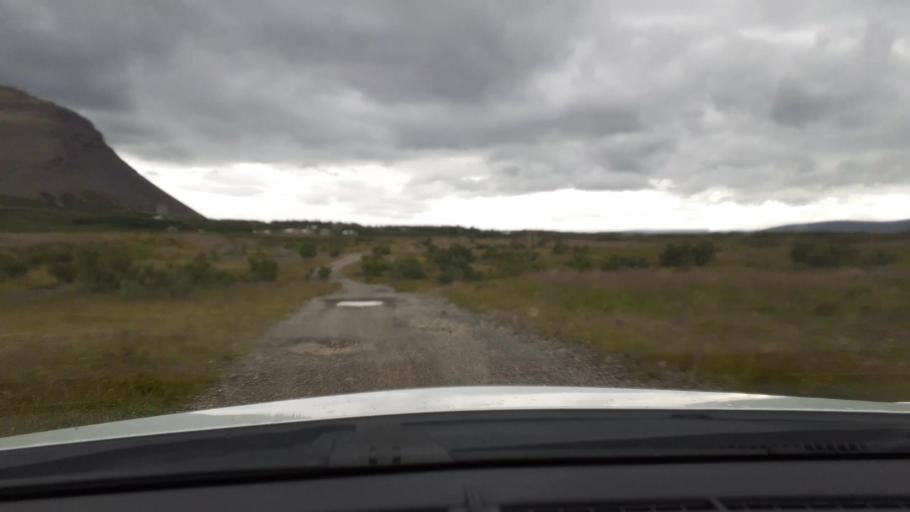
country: IS
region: West
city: Borgarnes
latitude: 64.4635
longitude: -21.9611
